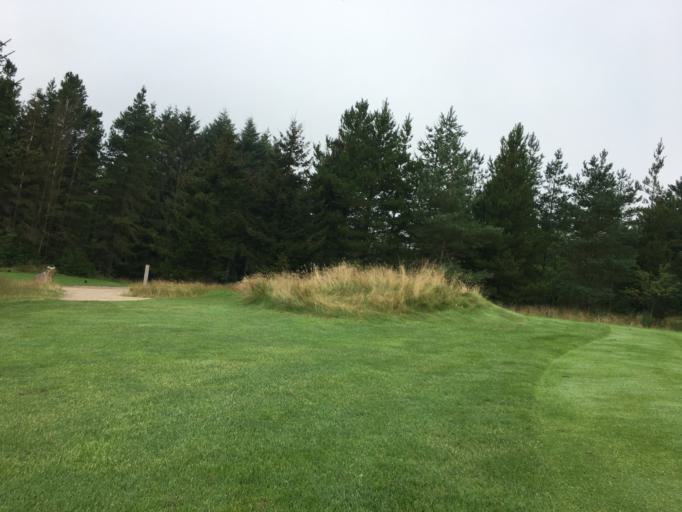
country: DK
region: Central Jutland
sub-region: Holstebro Kommune
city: Ulfborg
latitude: 56.3272
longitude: 8.4264
